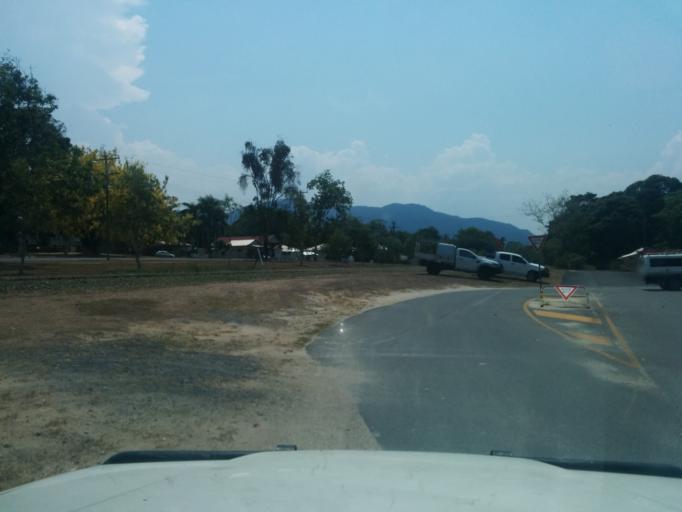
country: AU
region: Queensland
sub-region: Cairns
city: Redlynch
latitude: -16.8749
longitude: 145.7328
